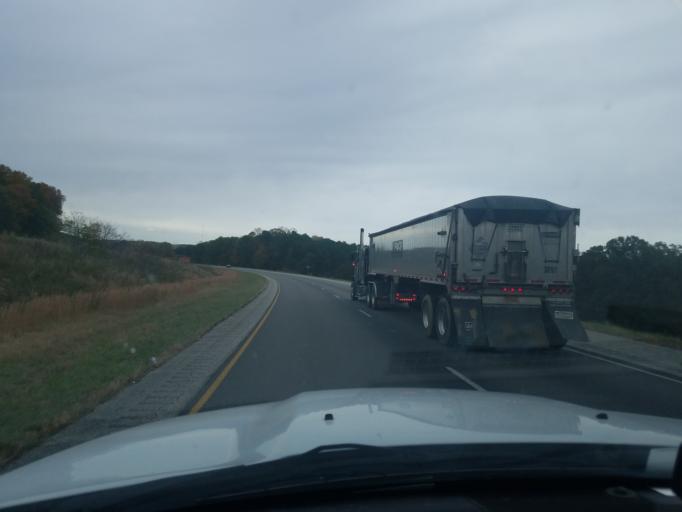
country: US
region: Indiana
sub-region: Crawford County
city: English
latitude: 38.2284
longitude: -86.5725
